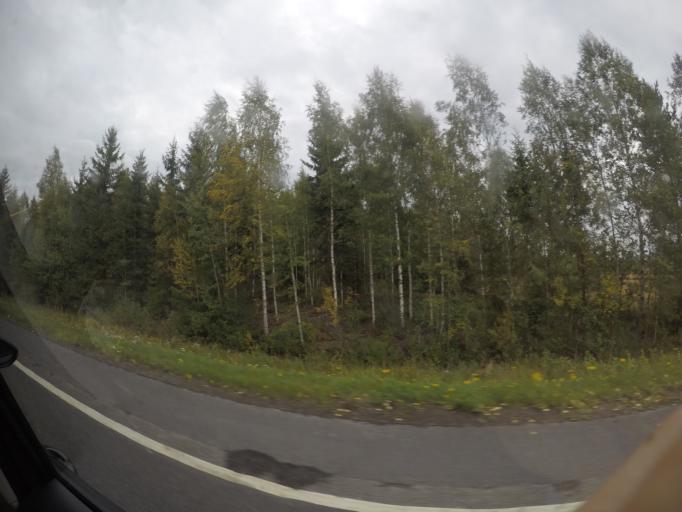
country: FI
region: Haeme
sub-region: Haemeenlinna
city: Parola
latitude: 61.1186
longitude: 24.4172
